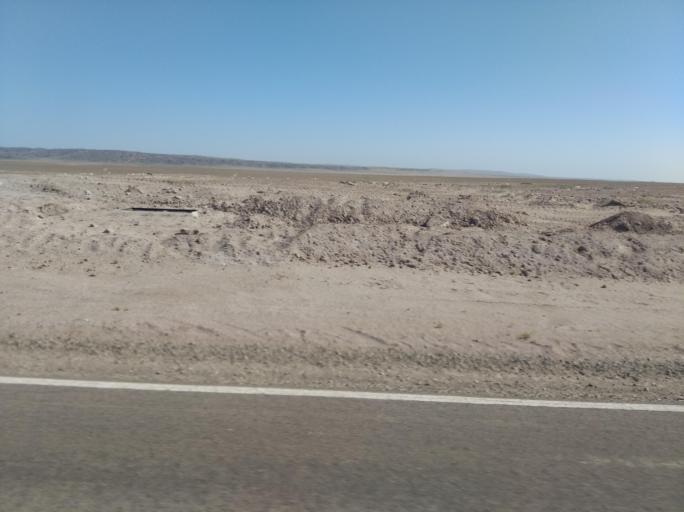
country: CL
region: Atacama
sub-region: Provincia de Copiapo
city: Copiapo
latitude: -27.3268
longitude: -70.8003
